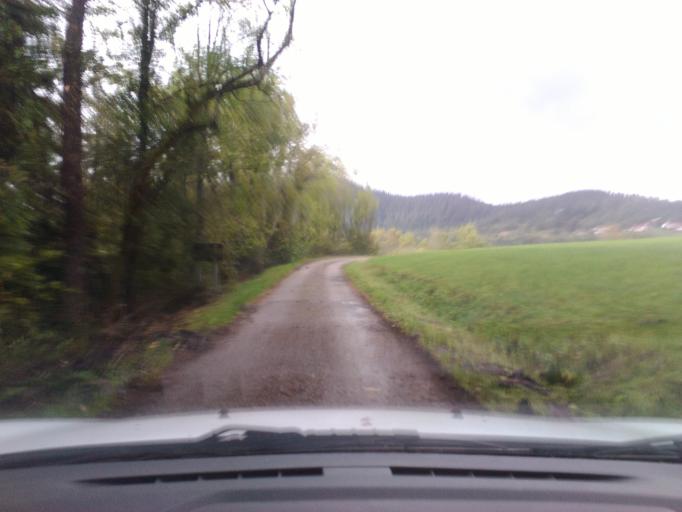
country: FR
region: Lorraine
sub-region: Departement des Vosges
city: Saint-Die-des-Vosges
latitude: 48.3055
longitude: 6.9731
